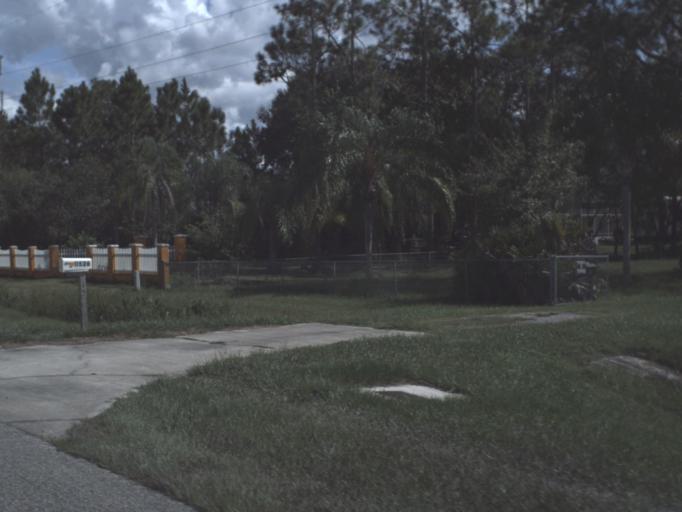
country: US
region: Florida
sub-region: Polk County
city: Babson Park
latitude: 27.8757
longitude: -81.4043
